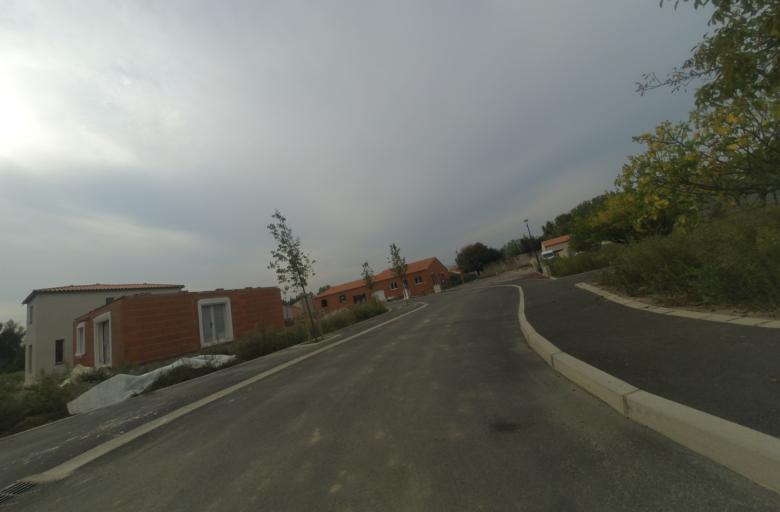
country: FR
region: Languedoc-Roussillon
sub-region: Departement des Pyrenees-Orientales
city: Millas
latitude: 42.6935
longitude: 2.7010
